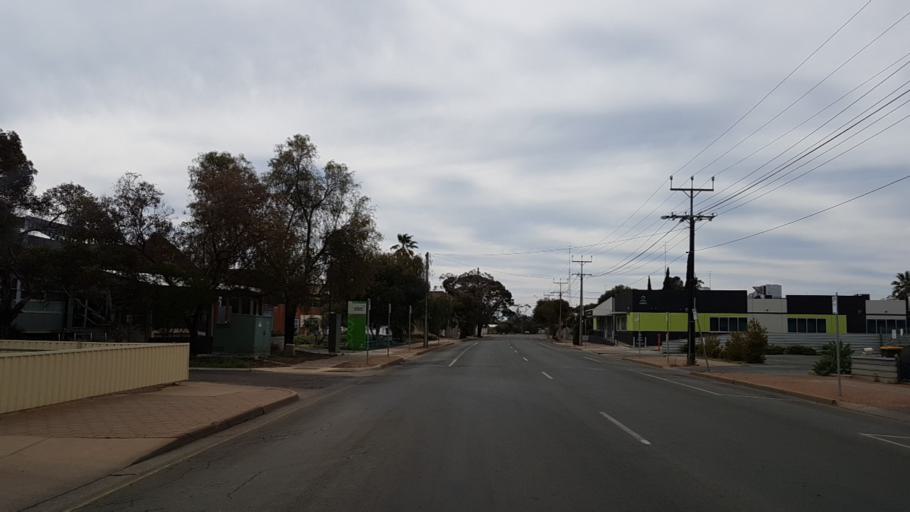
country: AU
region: South Australia
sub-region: Port Pirie City and Dists
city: Port Pirie
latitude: -33.1772
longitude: 138.0069
